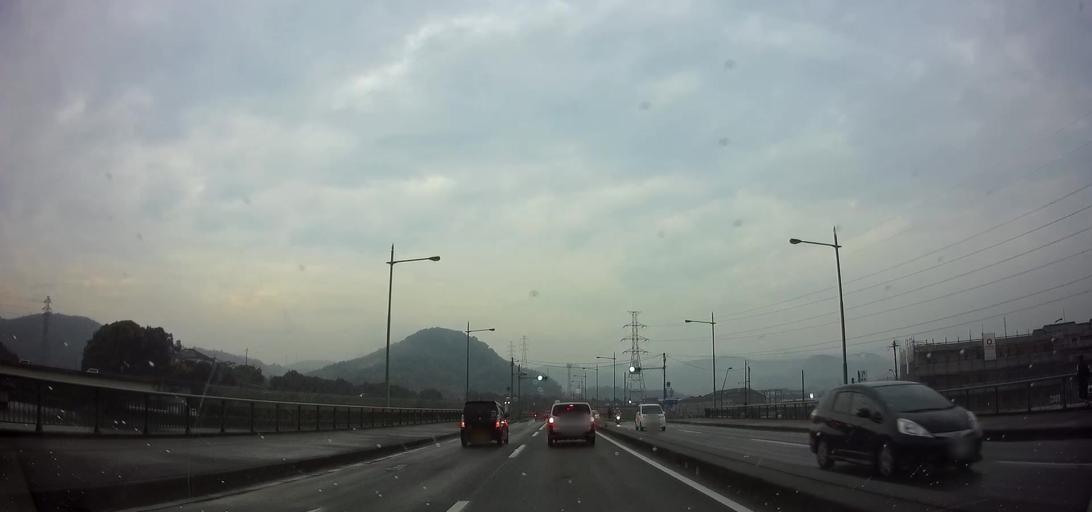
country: JP
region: Nagasaki
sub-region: Isahaya-shi
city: Isahaya
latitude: 32.8469
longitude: 130.0109
